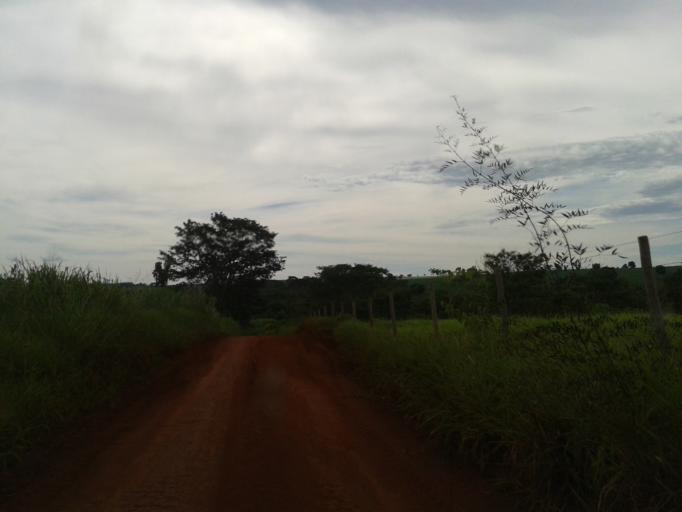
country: BR
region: Minas Gerais
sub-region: Centralina
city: Centralina
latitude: -18.6893
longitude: -49.3666
